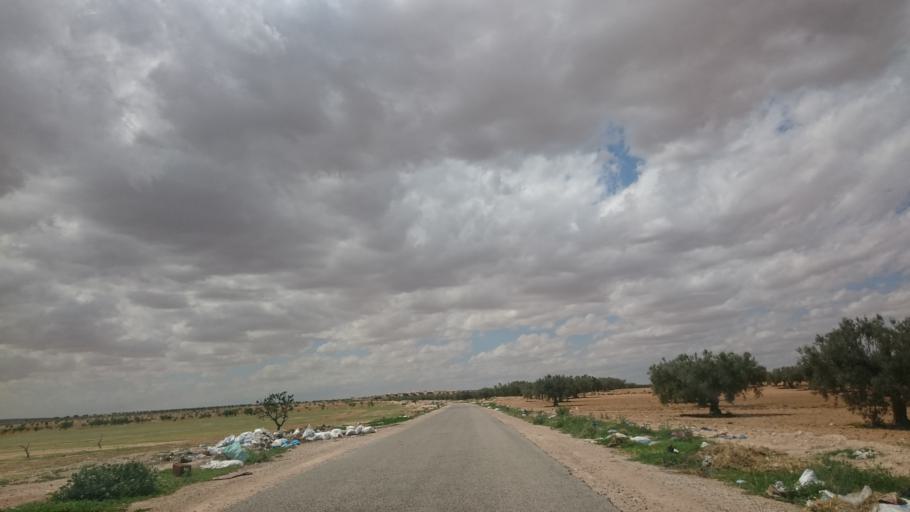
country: TN
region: Safaqis
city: Sfax
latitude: 34.7484
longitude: 10.5080
